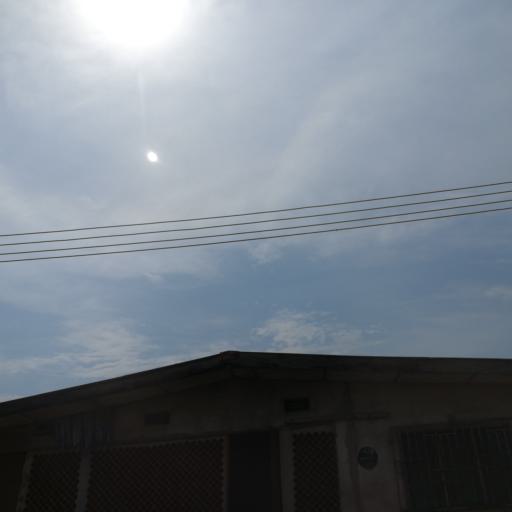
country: NG
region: Rivers
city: Port Harcourt
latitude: 4.8660
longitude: 7.0220
